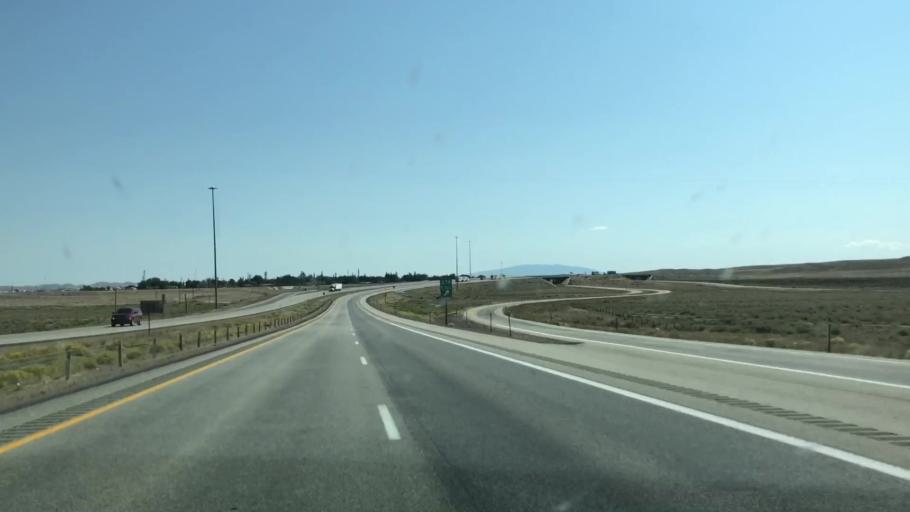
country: US
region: Wyoming
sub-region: Carbon County
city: Rawlins
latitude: 41.7815
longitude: -107.1364
